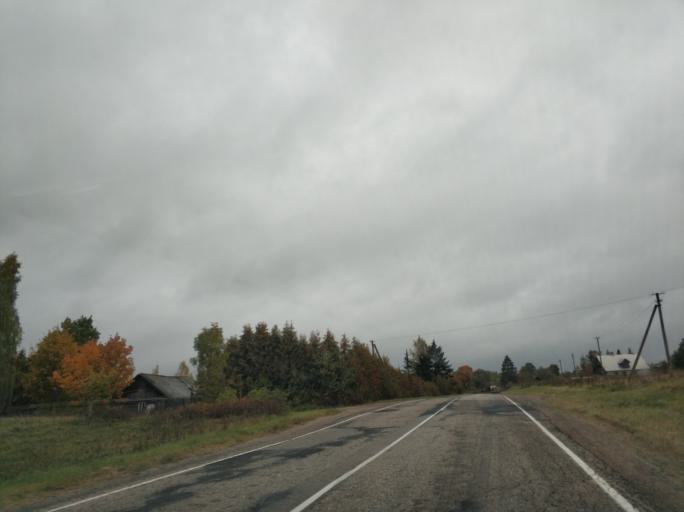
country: RU
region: Pskov
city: Sebezh
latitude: 56.2884
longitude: 28.5842
